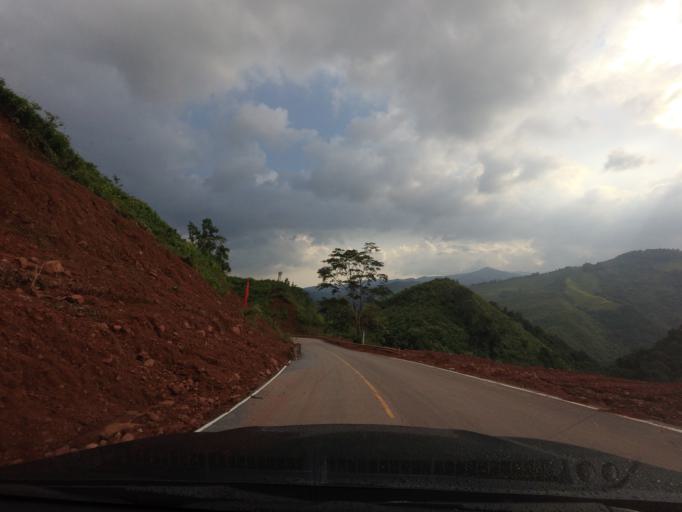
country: TH
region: Nan
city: Bo Kluea
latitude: 19.2592
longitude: 101.1796
